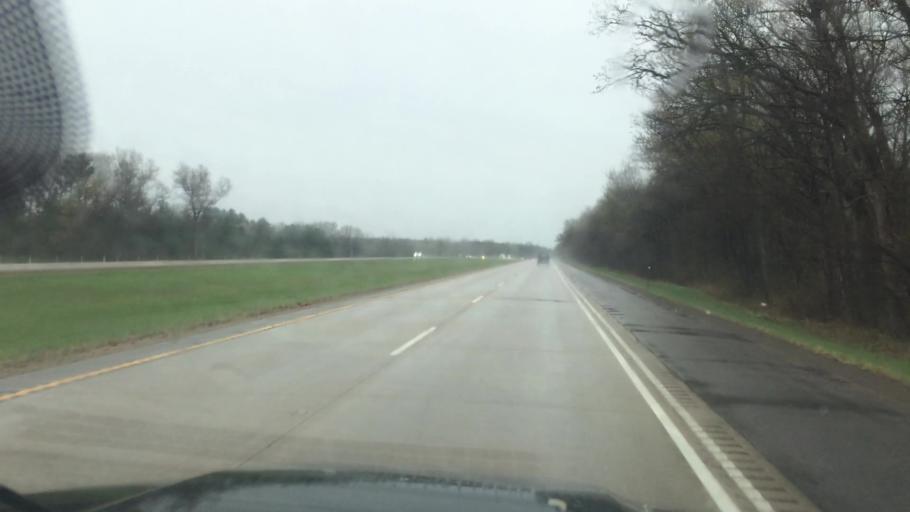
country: US
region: Wisconsin
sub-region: Portage County
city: Stevens Point
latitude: 44.6519
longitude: -89.6395
